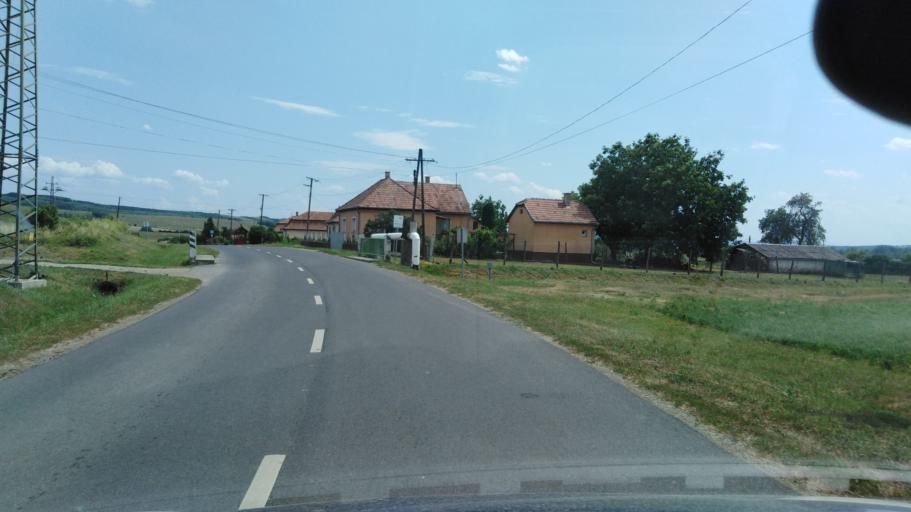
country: HU
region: Nograd
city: Szecseny
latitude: 48.1771
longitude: 19.5249
